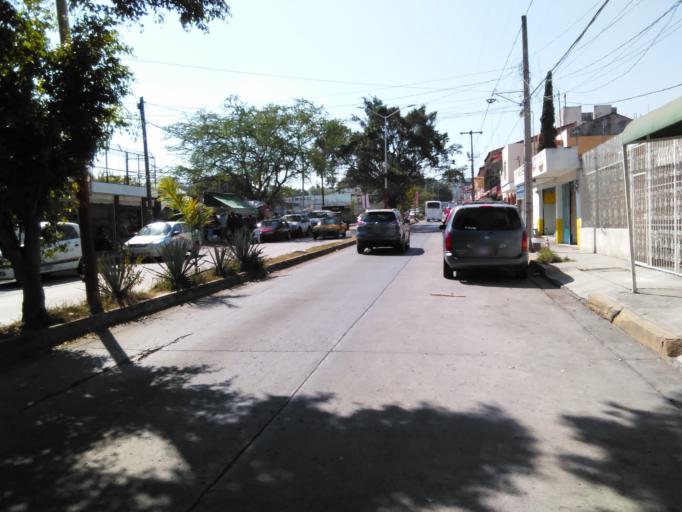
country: MX
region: Nayarit
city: Tepic
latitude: 21.4967
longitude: -104.8932
